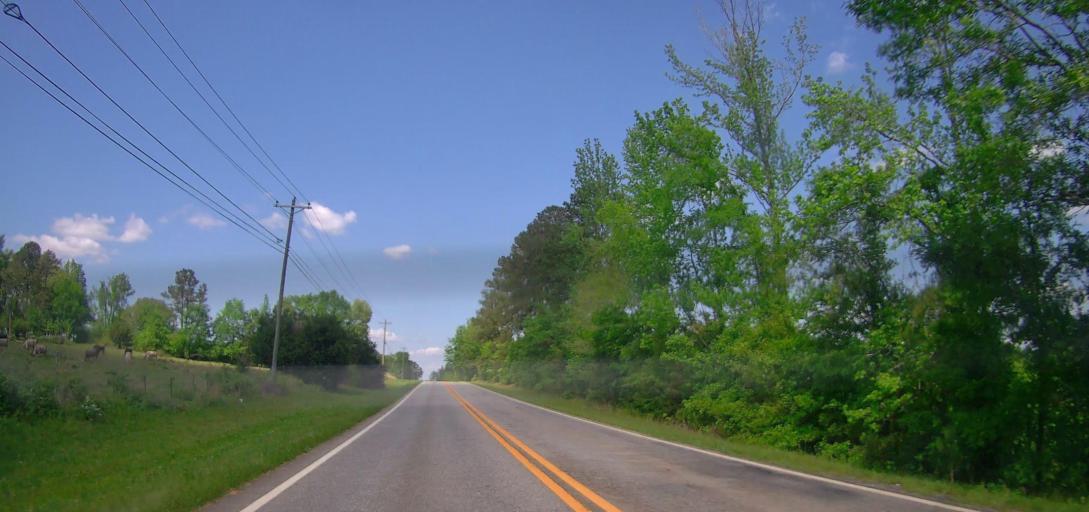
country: US
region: Georgia
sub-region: Putnam County
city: Eatonton
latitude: 33.3222
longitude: -83.2969
